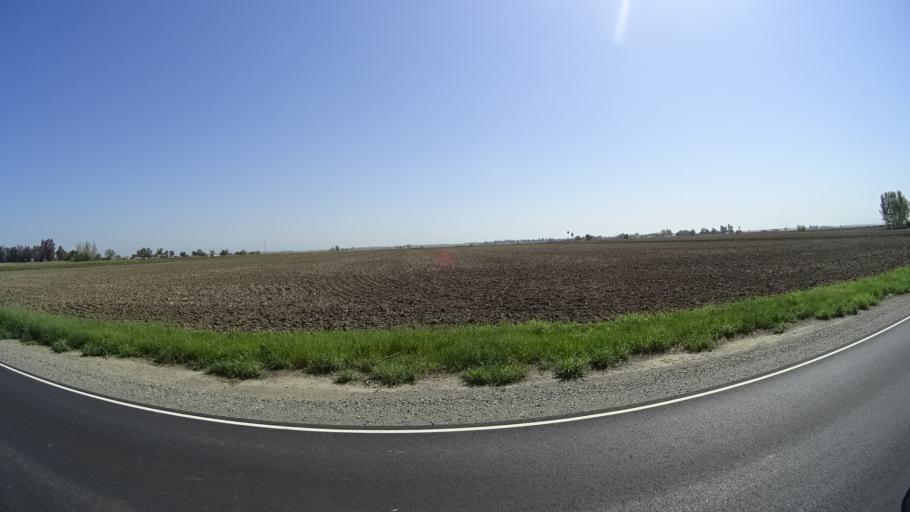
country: US
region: California
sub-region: Glenn County
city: Willows
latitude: 39.5897
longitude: -122.0655
